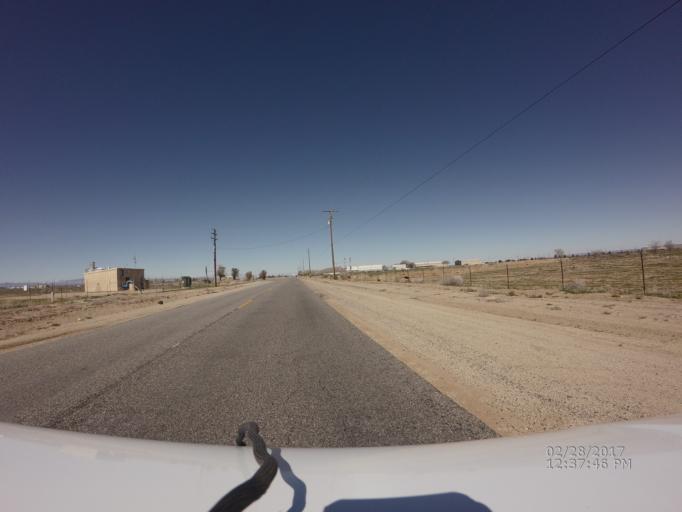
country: US
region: California
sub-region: Los Angeles County
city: Palmdale
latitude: 34.5980
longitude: -118.0854
